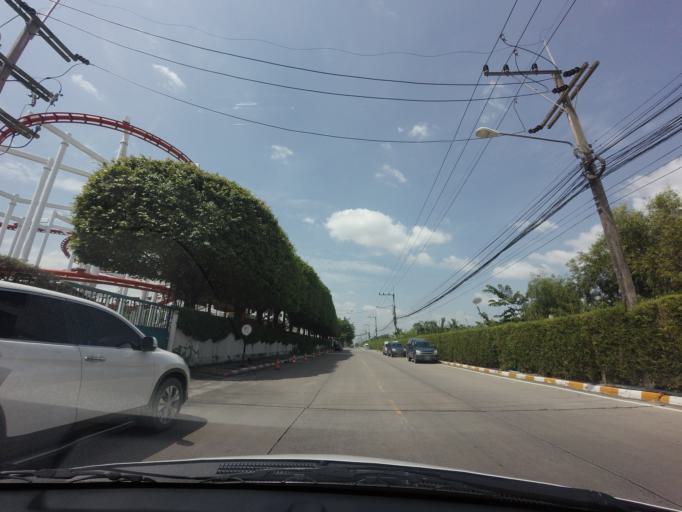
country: TH
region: Pathum Thani
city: Thanyaburi
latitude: 13.9936
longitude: 100.6747
